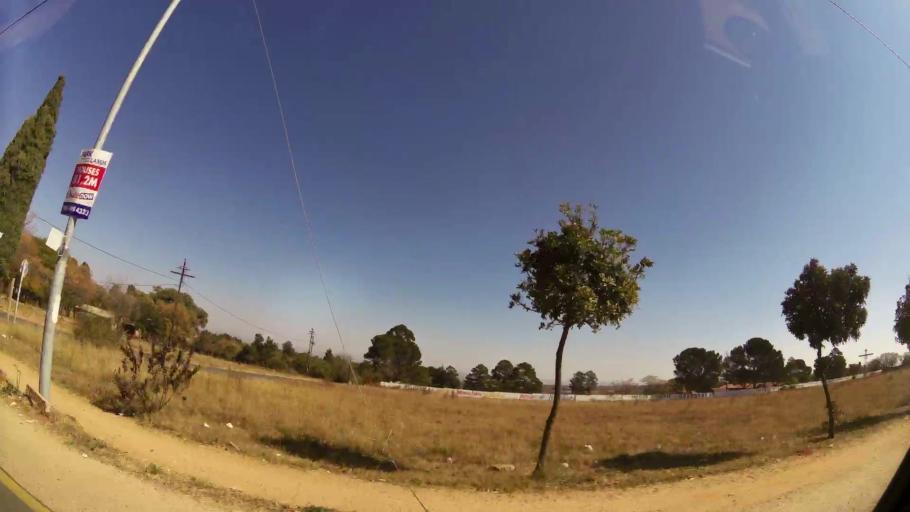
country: ZA
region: Gauteng
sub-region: City of Johannesburg Metropolitan Municipality
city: Midrand
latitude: -25.9468
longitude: 28.0977
